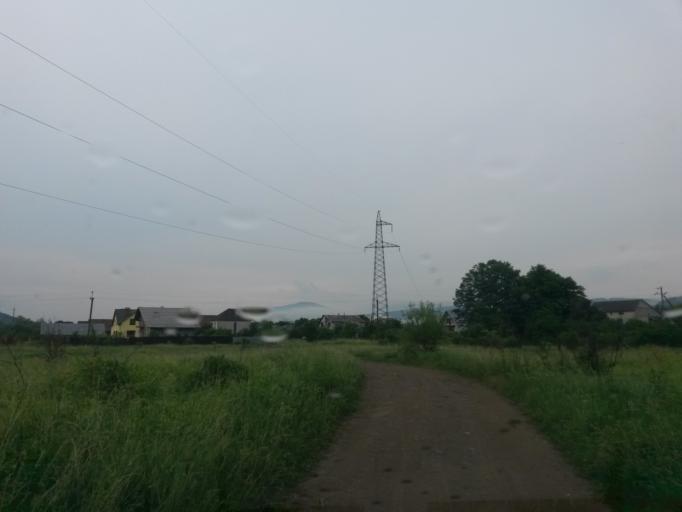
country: UA
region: Zakarpattia
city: Velykyi Bereznyi
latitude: 48.9068
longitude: 22.4658
